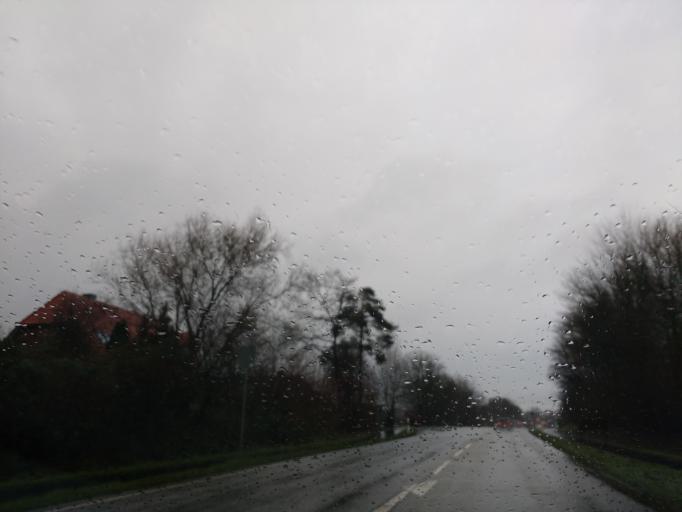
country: DE
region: Schleswig-Holstein
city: Holzbunge
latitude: 54.3768
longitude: 9.7046
